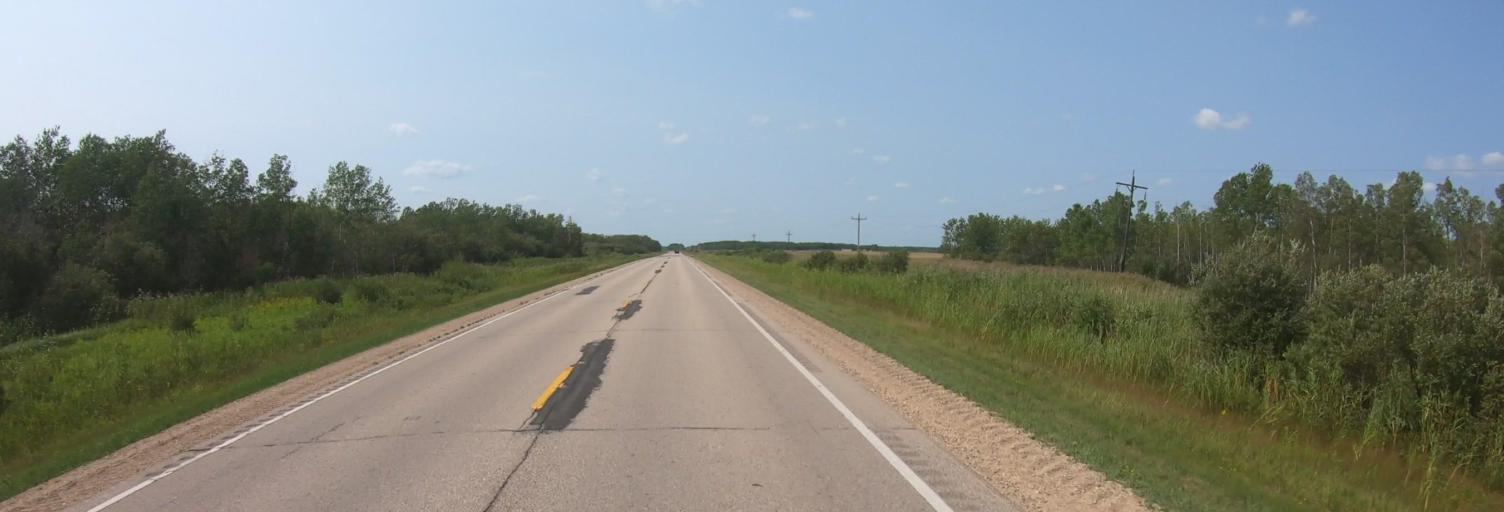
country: US
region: Minnesota
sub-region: Lake of the Woods County
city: Baudette
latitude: 48.7335
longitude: -94.8084
